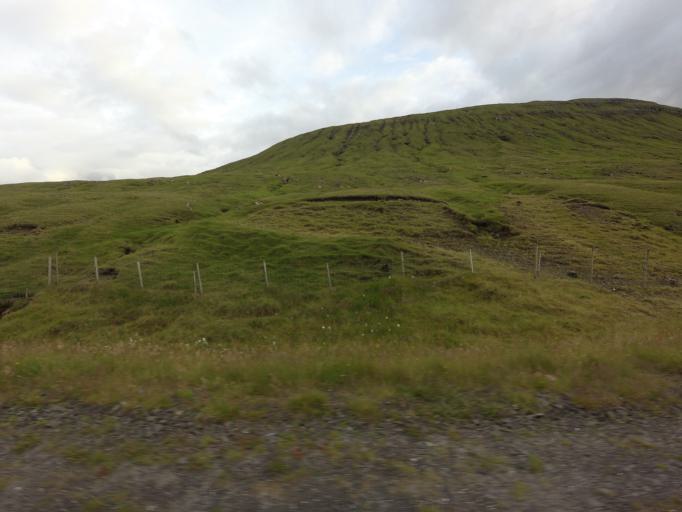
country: FO
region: Streymoy
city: Kollafjordhur
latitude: 62.1796
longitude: -6.9883
